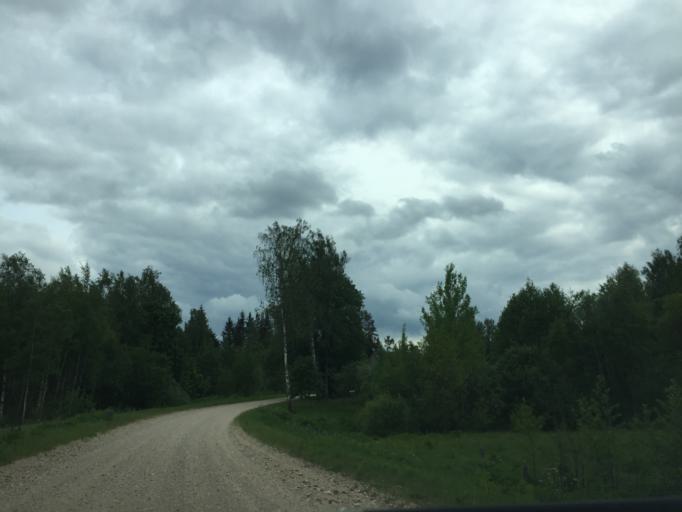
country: LV
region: Dagda
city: Dagda
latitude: 56.1851
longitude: 27.2892
